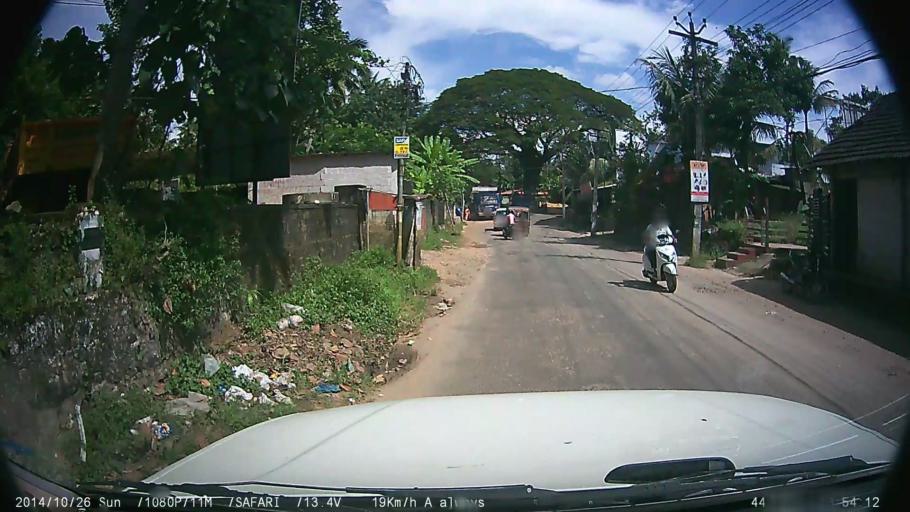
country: IN
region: Kerala
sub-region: Kottayam
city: Changanacheri
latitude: 9.4401
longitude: 76.5598
